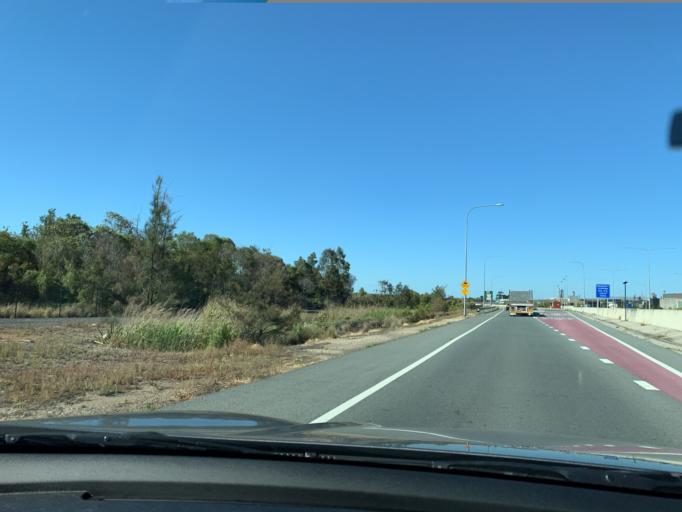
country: AU
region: Queensland
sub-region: Brisbane
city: Wynnum
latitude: -27.4294
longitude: 153.1433
